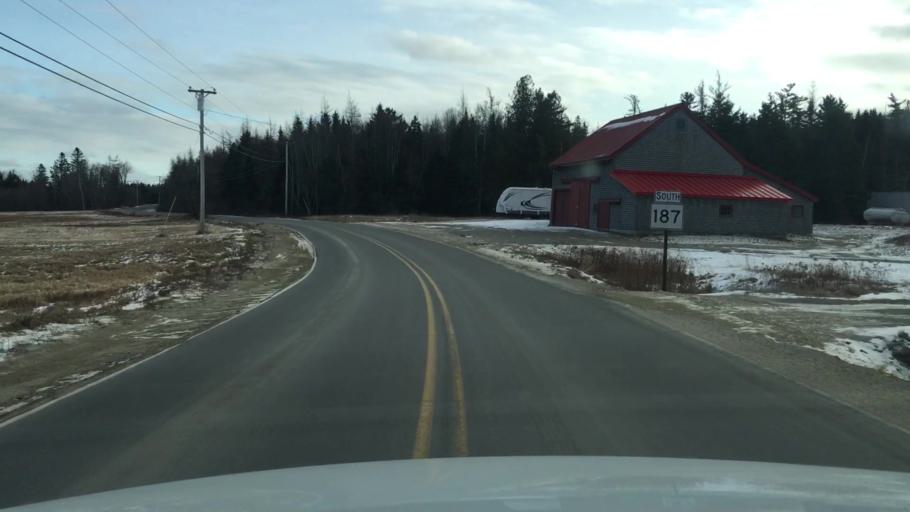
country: US
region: Maine
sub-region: Washington County
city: Jonesport
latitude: 44.6165
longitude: -67.6065
